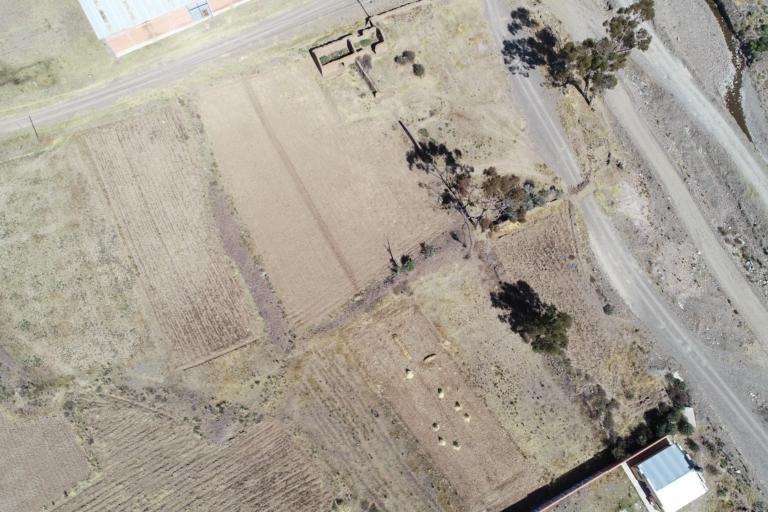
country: BO
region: La Paz
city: Achacachi
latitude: -15.8982
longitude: -68.9021
